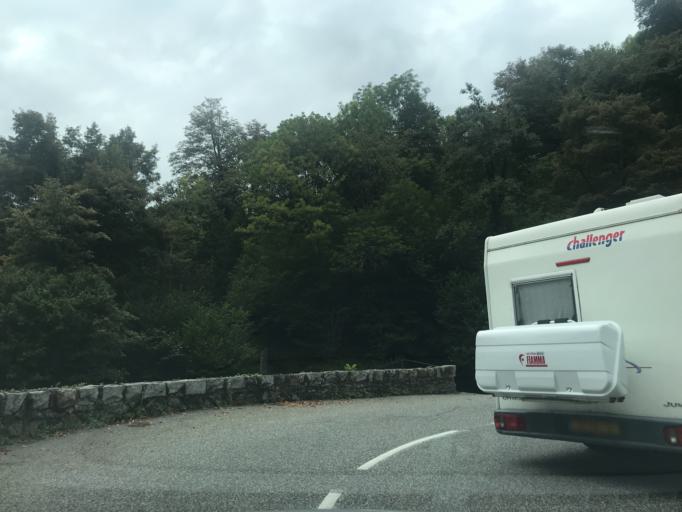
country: FR
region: Midi-Pyrenees
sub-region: Departement de la Haute-Garonne
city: Bagneres-de-Luchon
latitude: 42.7701
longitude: 0.6209
